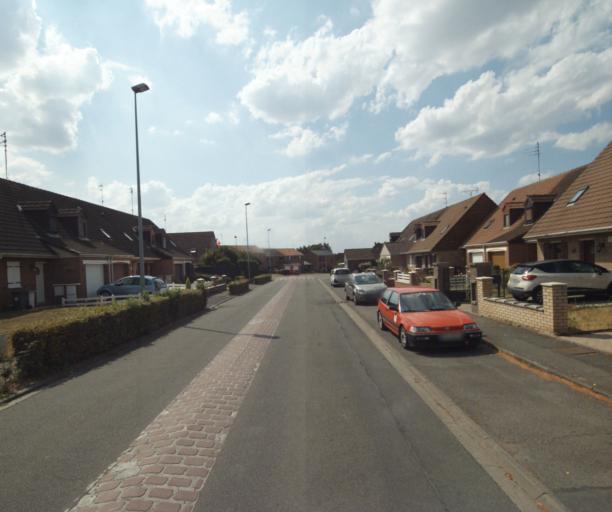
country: FR
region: Nord-Pas-de-Calais
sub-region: Departement du Nord
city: Neuville-en-Ferrain
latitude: 50.7402
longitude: 3.1608
